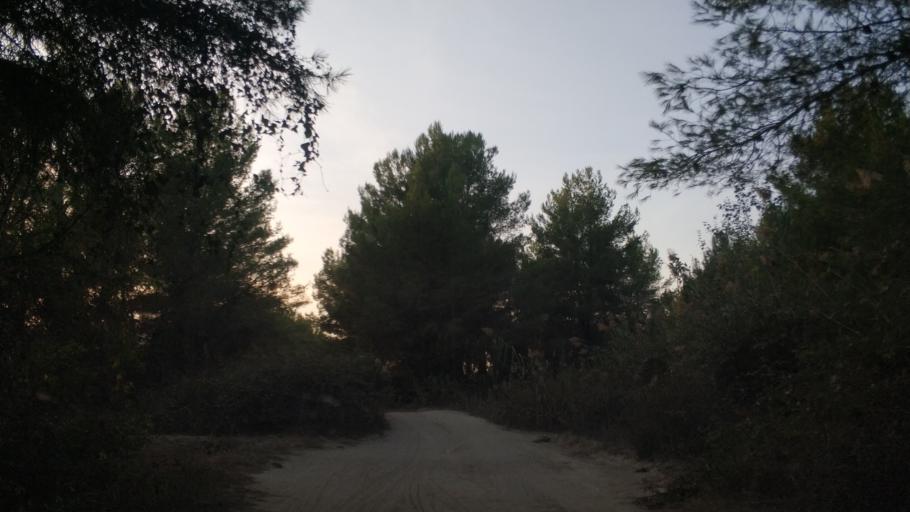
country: AL
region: Fier
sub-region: Rrethi i Lushnjes
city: Divjake
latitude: 40.9529
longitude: 19.4748
